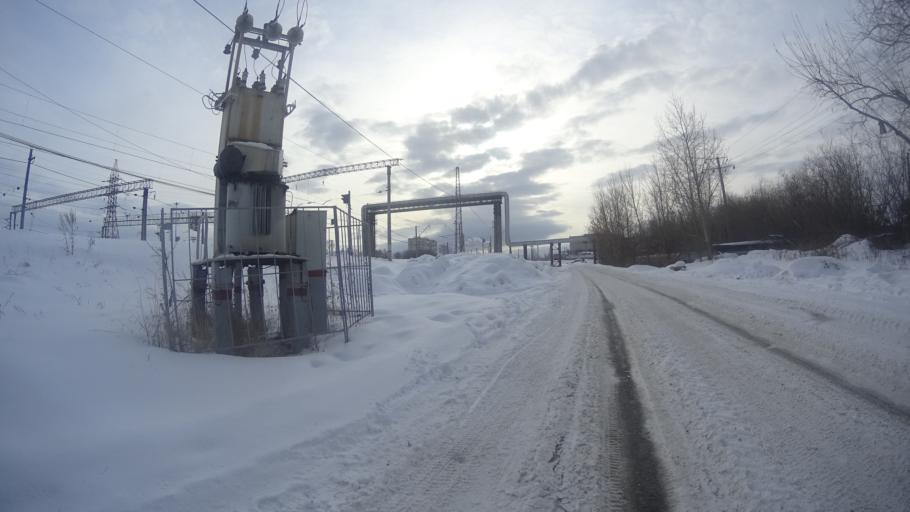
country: RU
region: Chelyabinsk
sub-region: Gorod Chelyabinsk
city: Chelyabinsk
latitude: 55.1273
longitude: 61.4013
